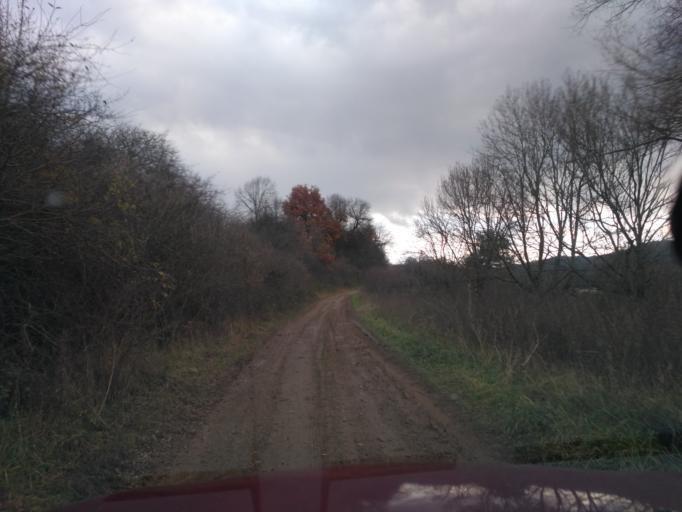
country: SK
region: Presovsky
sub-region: Okres Presov
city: Presov
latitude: 48.9272
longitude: 21.1956
